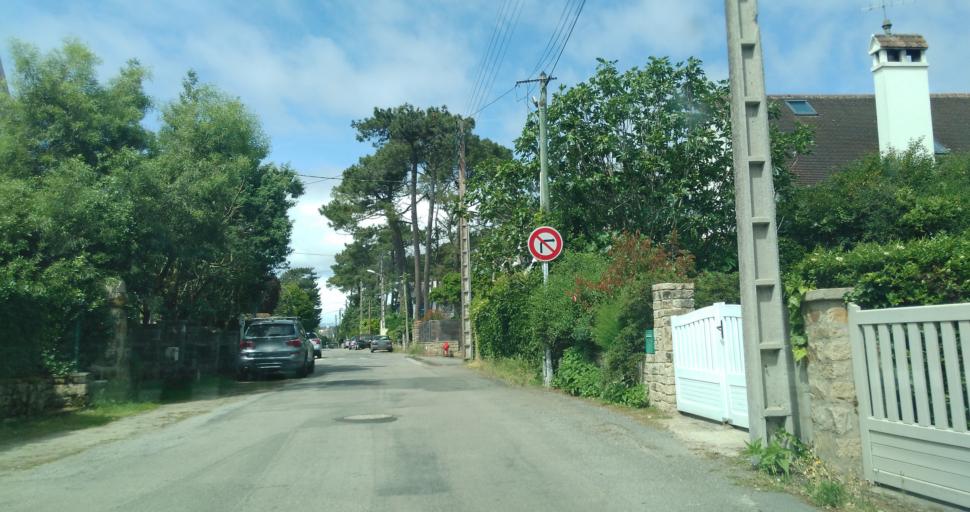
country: FR
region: Brittany
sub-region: Departement du Morbihan
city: Carnac
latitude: 47.5735
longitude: -3.0634
